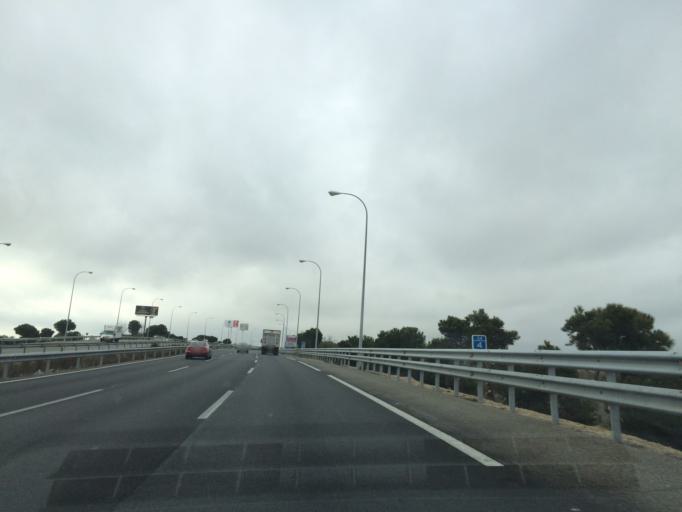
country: ES
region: Madrid
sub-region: Provincia de Madrid
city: Alcorcon
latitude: 40.3835
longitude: -3.8171
